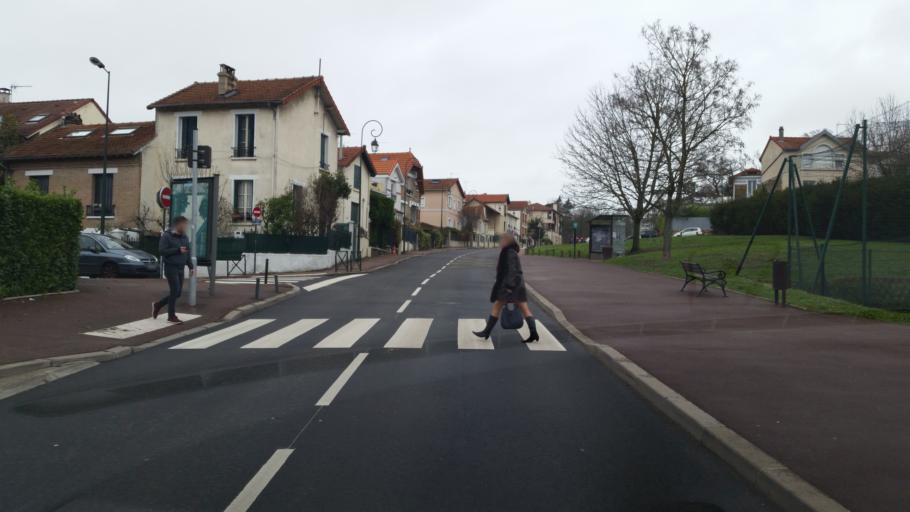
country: FR
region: Ile-de-France
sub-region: Departement des Hauts-de-Seine
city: Saint-Cloud
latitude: 48.8451
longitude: 2.1982
